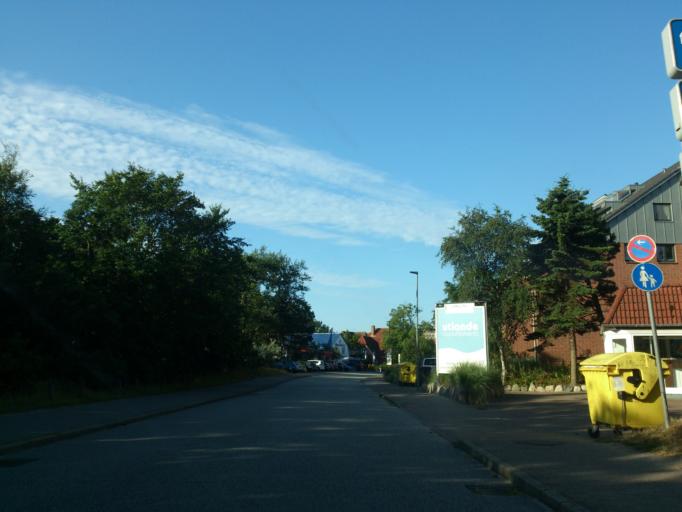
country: DE
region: Schleswig-Holstein
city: Sankt Peter-Ording
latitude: 54.3171
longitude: 8.6089
